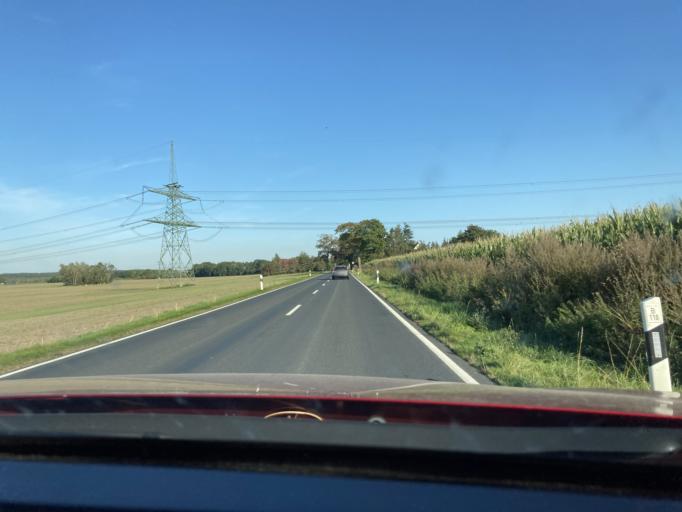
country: DE
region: Mecklenburg-Vorpommern
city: Jarmen
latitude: 53.8861
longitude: 13.4511
